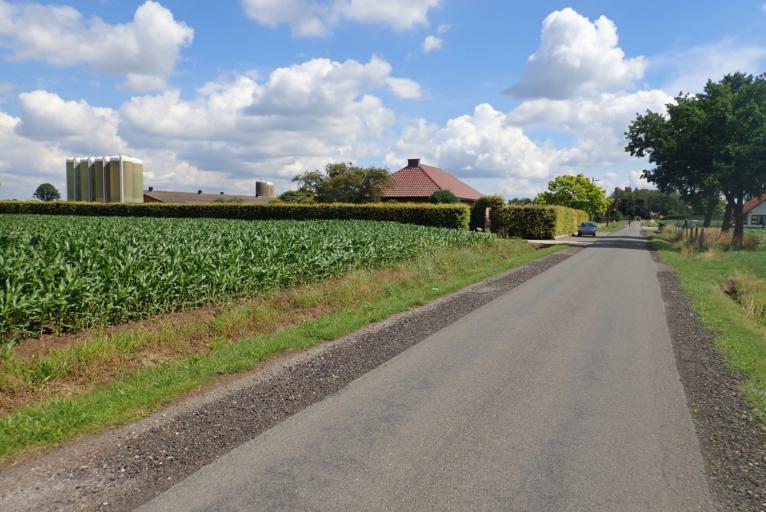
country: BE
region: Flanders
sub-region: Provincie Antwerpen
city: Oostmalle
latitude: 51.3178
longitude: 4.7548
